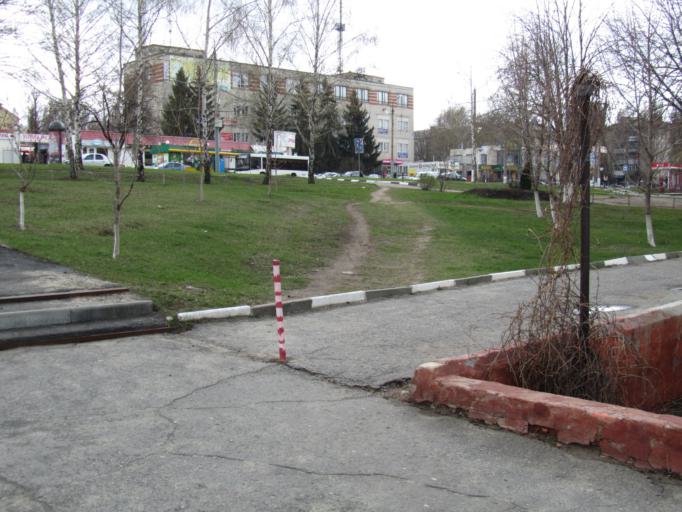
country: RU
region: Belgorod
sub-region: Belgorodskiy Rayon
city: Belgorod
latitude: 50.5792
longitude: 36.5820
